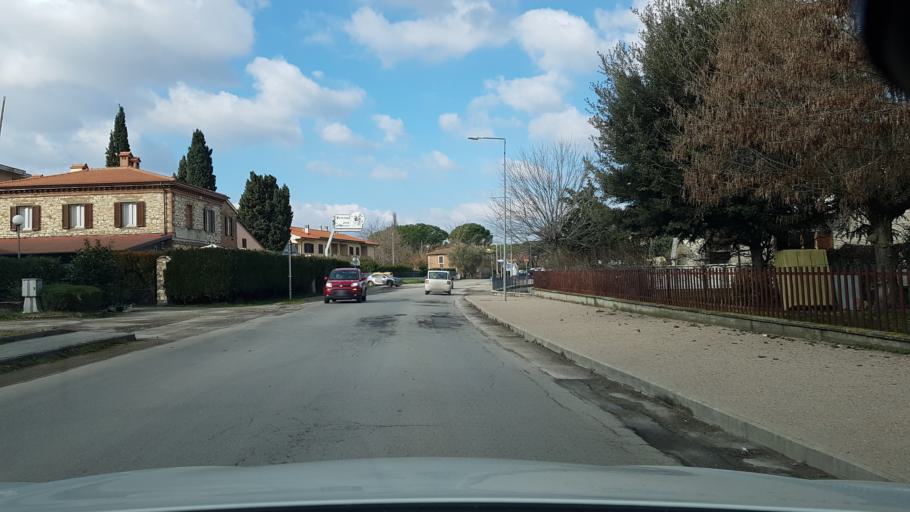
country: IT
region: Umbria
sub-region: Provincia di Perugia
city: Castiglione del Lago
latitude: 43.1288
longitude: 12.0458
